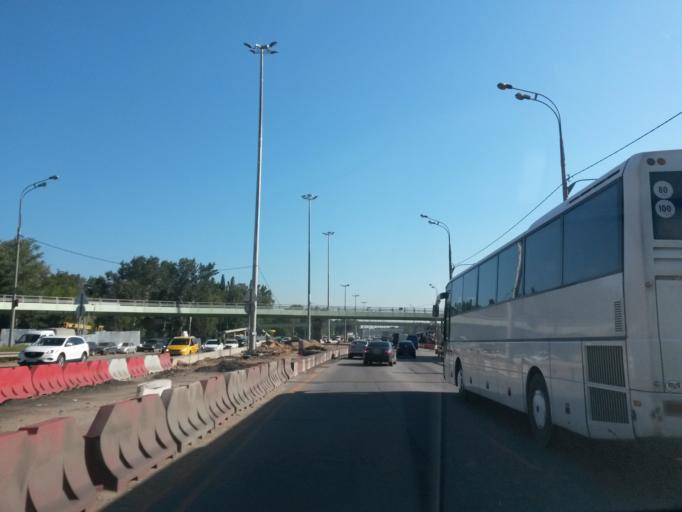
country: RU
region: Moskovskaya
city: Bolshevo
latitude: 55.9300
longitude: 37.8035
